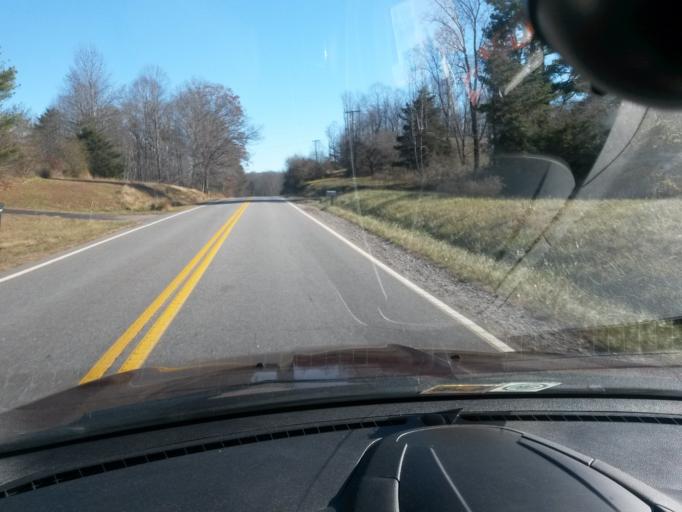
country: US
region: Virginia
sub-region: Patrick County
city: Patrick Springs
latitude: 36.7677
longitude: -80.1608
